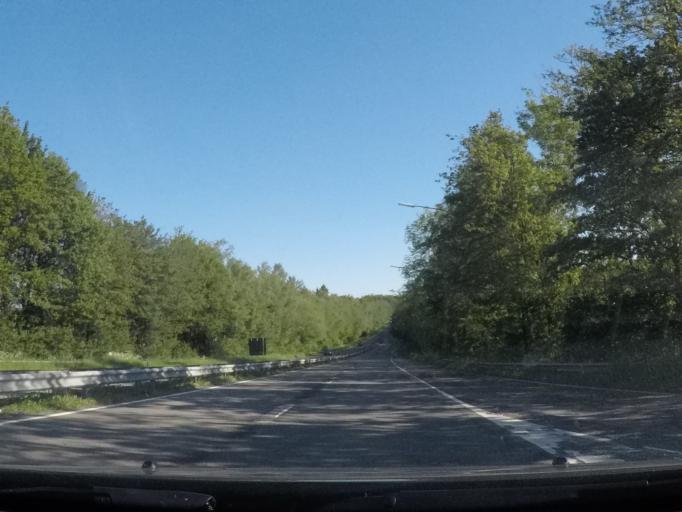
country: BE
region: Wallonia
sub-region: Province du Luxembourg
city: Saint-Hubert
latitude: 50.0107
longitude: 5.3826
